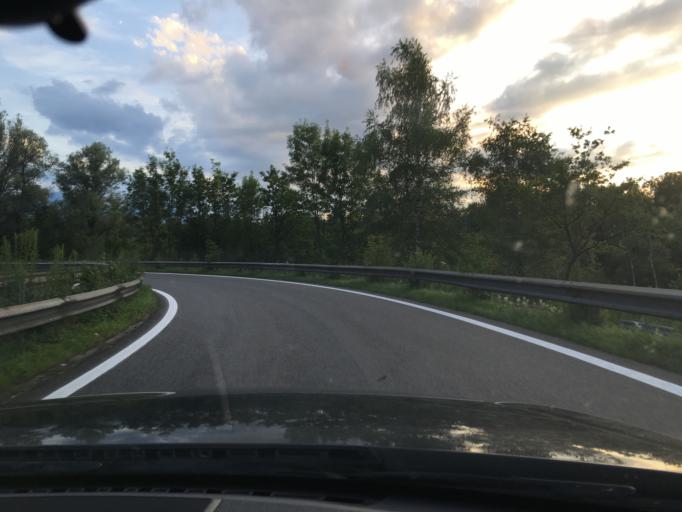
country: AT
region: Vorarlberg
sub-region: Politischer Bezirk Dornbirn
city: Hohenems
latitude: 47.3761
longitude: 9.6700
